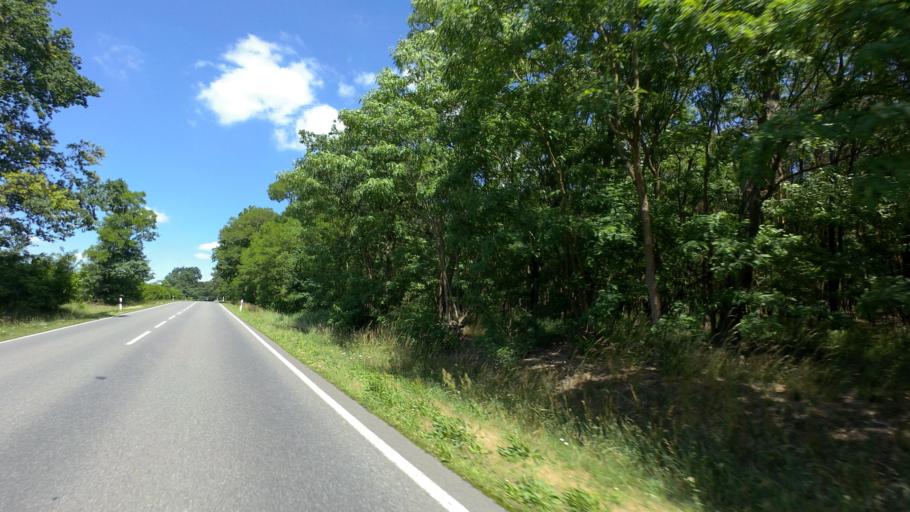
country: DE
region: Brandenburg
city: Kasel-Golzig
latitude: 51.9112
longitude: 13.6707
